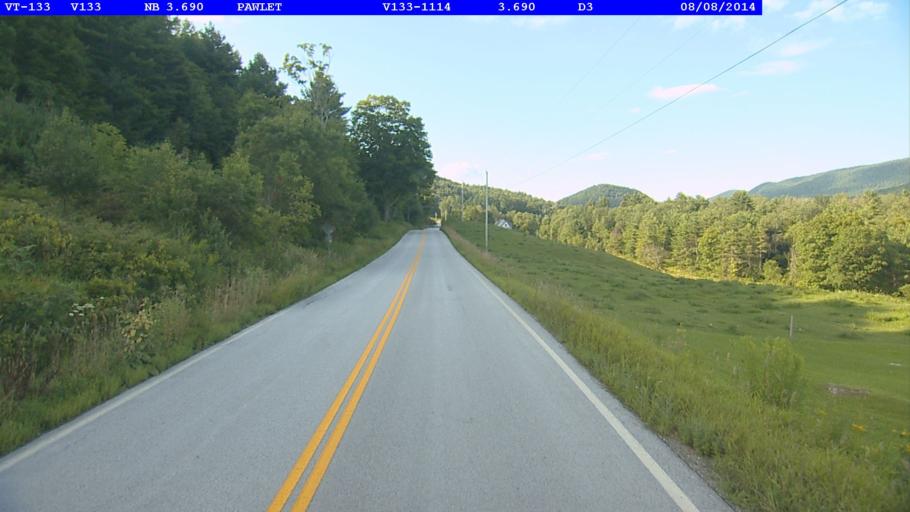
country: US
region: New York
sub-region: Washington County
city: Granville
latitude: 43.3829
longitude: -73.1373
